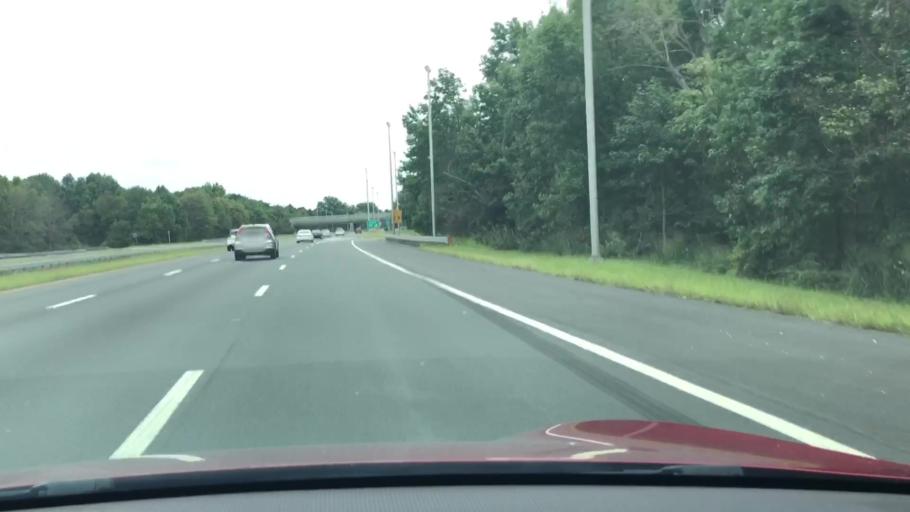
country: US
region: New Jersey
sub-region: Monmouth County
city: Shrewsbury
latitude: 40.1788
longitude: -74.5165
